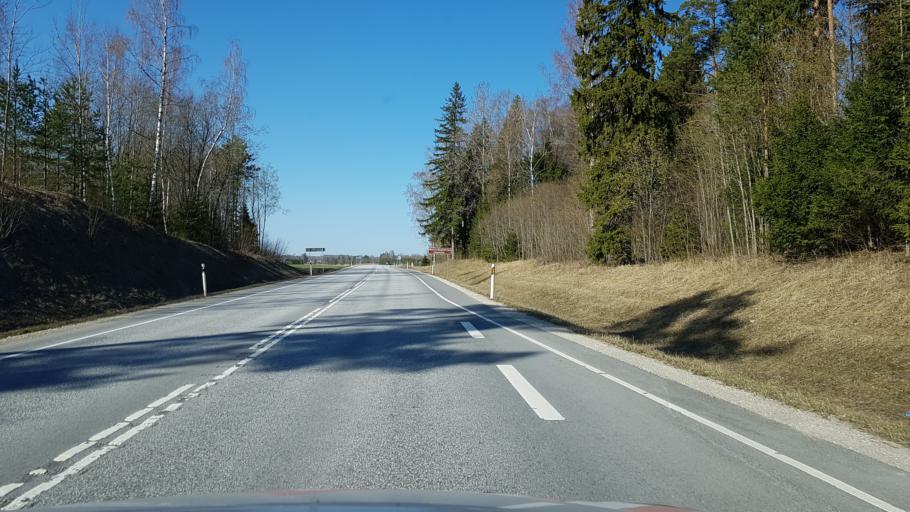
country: EE
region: Tartu
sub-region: Tartu linn
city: Tartu
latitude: 58.5200
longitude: 26.7695
